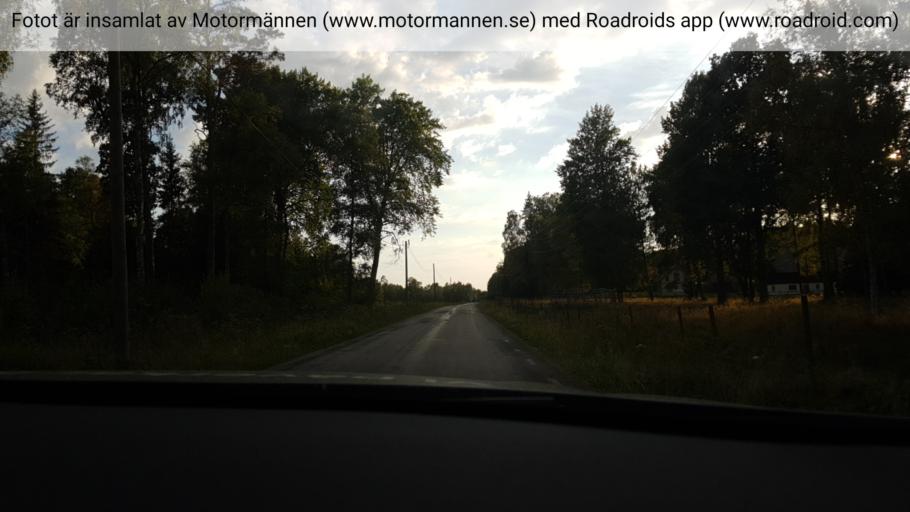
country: SE
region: Vaestra Goetaland
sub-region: Falkopings Kommun
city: Floby
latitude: 57.9933
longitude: 13.4438
